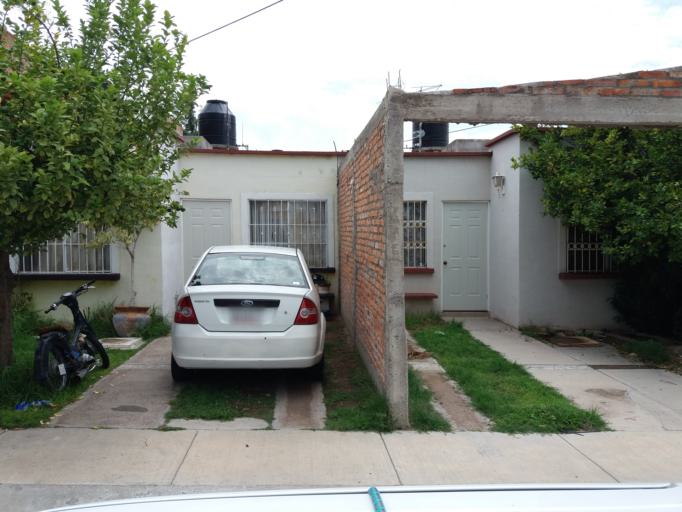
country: MX
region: Aguascalientes
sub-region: Aguascalientes
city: San Sebastian [Fraccionamiento]
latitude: 21.8203
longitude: -102.2679
